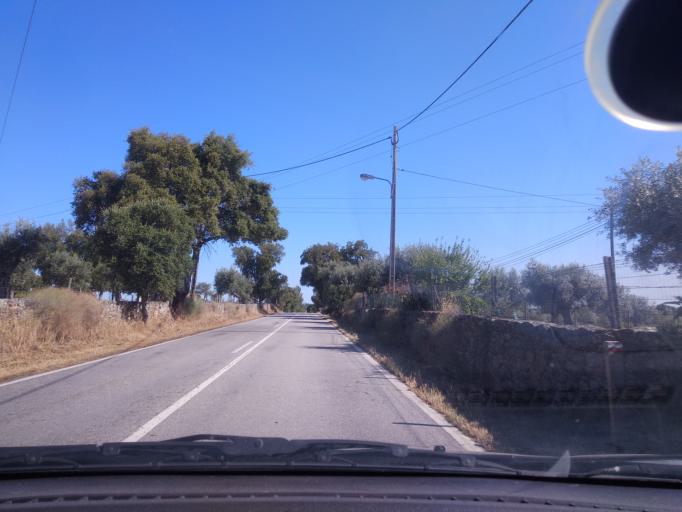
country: PT
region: Portalegre
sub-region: Nisa
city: Nisa
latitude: 39.4269
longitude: -7.6213
